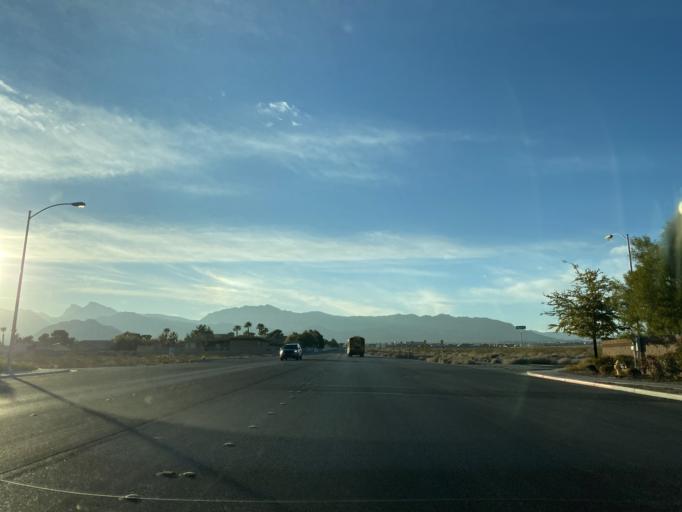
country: US
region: Nevada
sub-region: Clark County
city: Summerlin South
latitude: 36.2773
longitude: -115.3009
